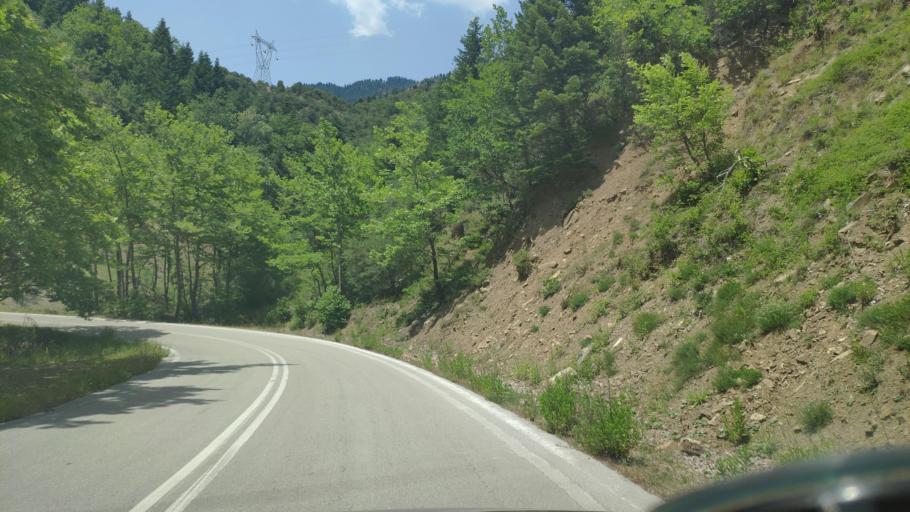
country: GR
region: Thessaly
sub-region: Nomos Kardhitsas
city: Anthiro
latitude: 39.2707
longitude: 21.3539
